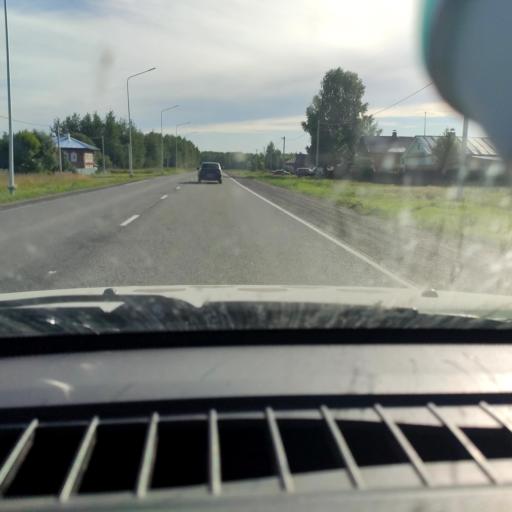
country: RU
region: Kirov
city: Vakhrushi
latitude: 58.6695
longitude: 49.9386
